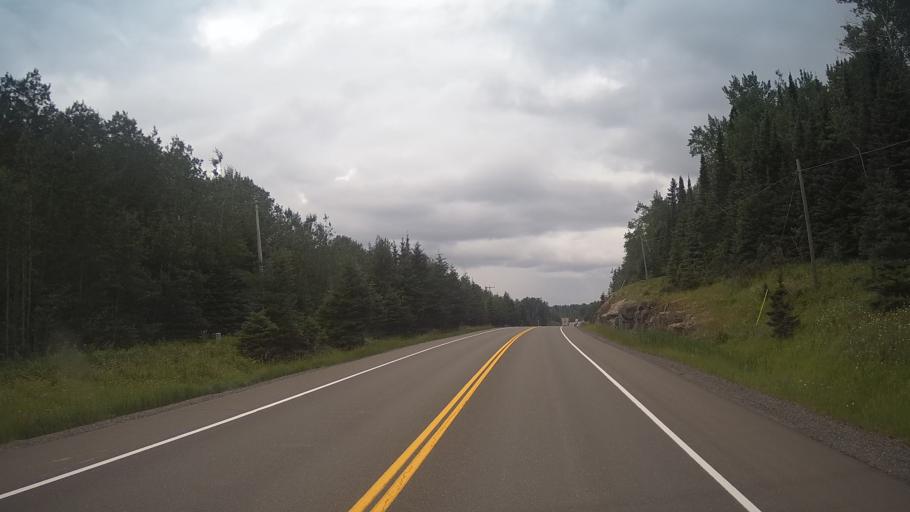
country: CA
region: Ontario
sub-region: Thunder Bay District
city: Thunder Bay
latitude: 48.5082
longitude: -89.4642
